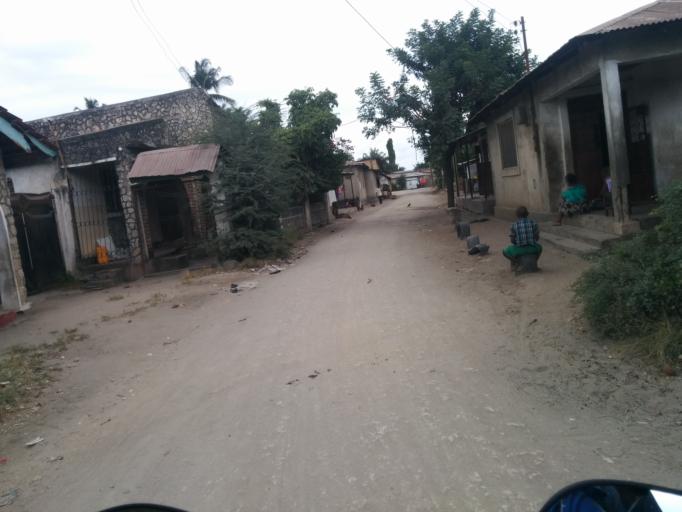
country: TZ
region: Dar es Salaam
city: Dar es Salaam
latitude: -6.8686
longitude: 39.2468
